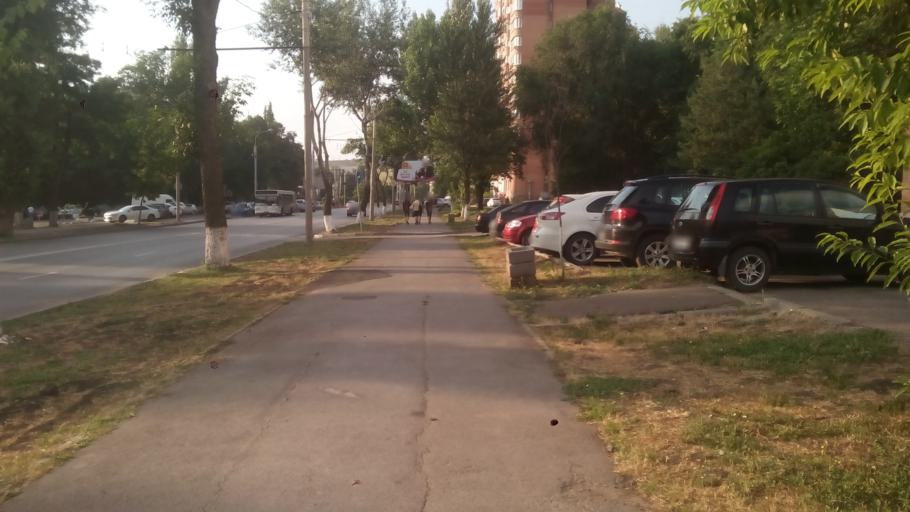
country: RU
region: Rostov
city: Imeni Chkalova
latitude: 47.2482
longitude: 39.7651
